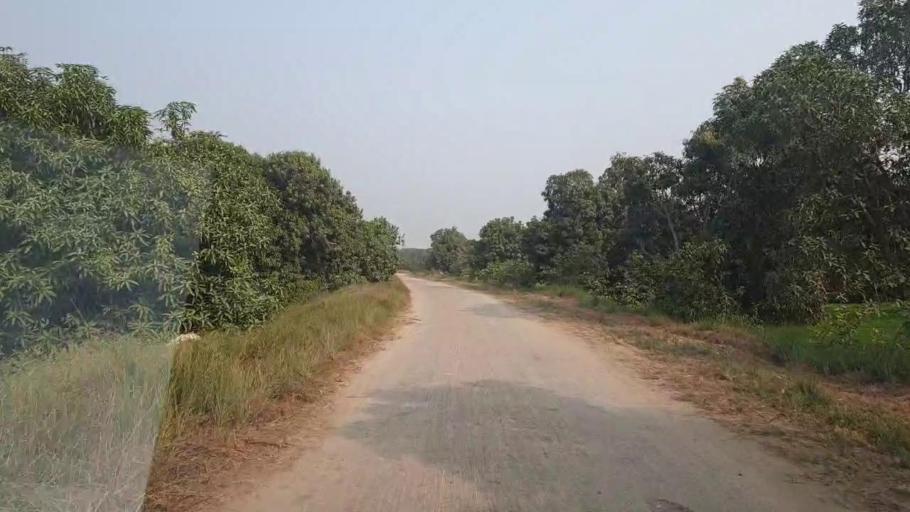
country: PK
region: Sindh
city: Tando Jam
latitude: 25.3323
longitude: 68.5180
